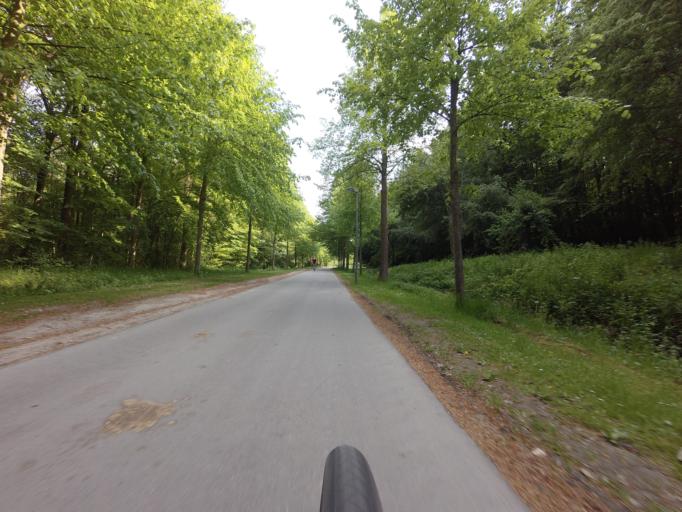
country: DK
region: Capital Region
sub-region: Brondby Kommune
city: Brondbyvester
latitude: 55.6475
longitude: 12.4274
